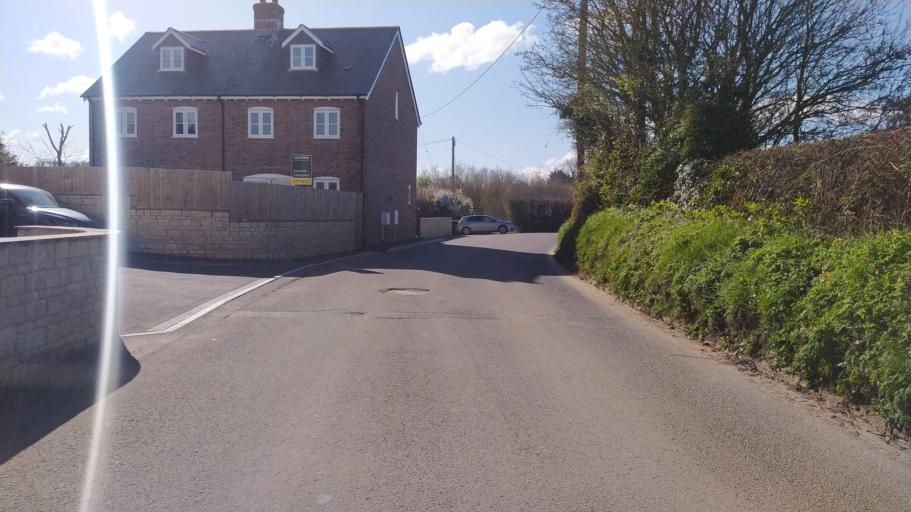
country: GB
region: England
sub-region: Dorset
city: Sturminster Newton
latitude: 50.9616
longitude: -2.3256
